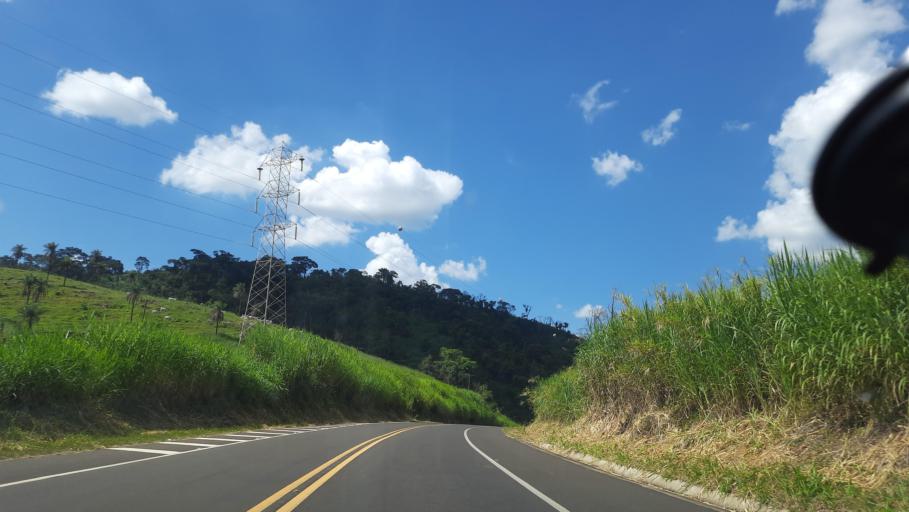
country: BR
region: Sao Paulo
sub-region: Sao Jose Do Rio Pardo
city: Sao Jose do Rio Pardo
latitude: -21.6056
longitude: -46.9615
